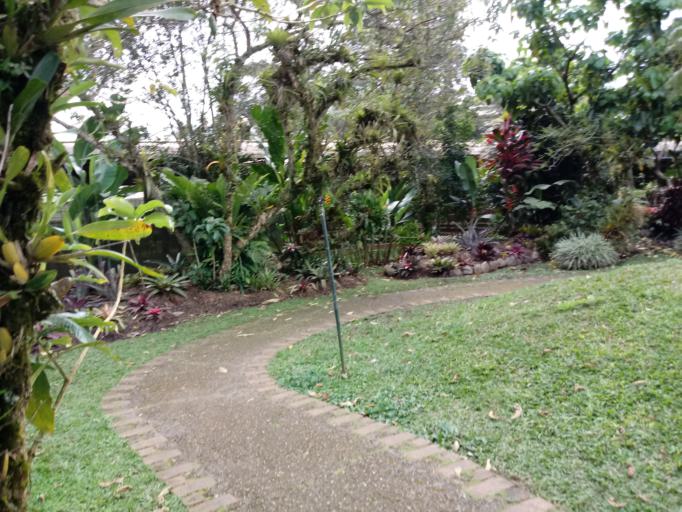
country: CR
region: Cartago
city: Paraiso
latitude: 9.8394
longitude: -83.8881
